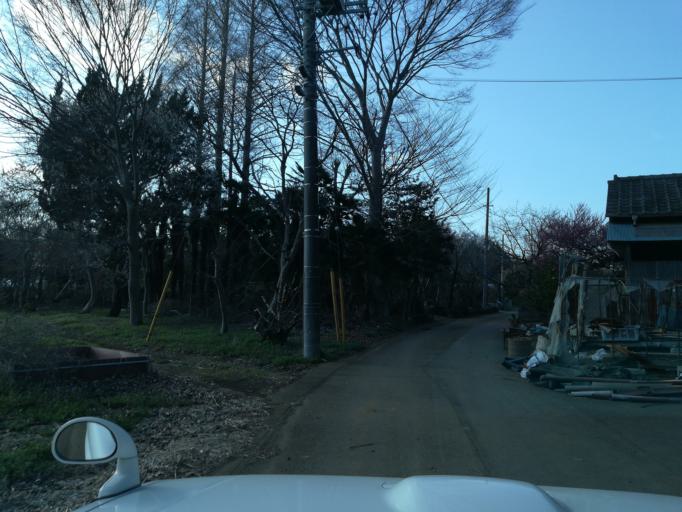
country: JP
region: Ibaraki
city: Naka
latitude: 36.0898
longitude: 140.0892
